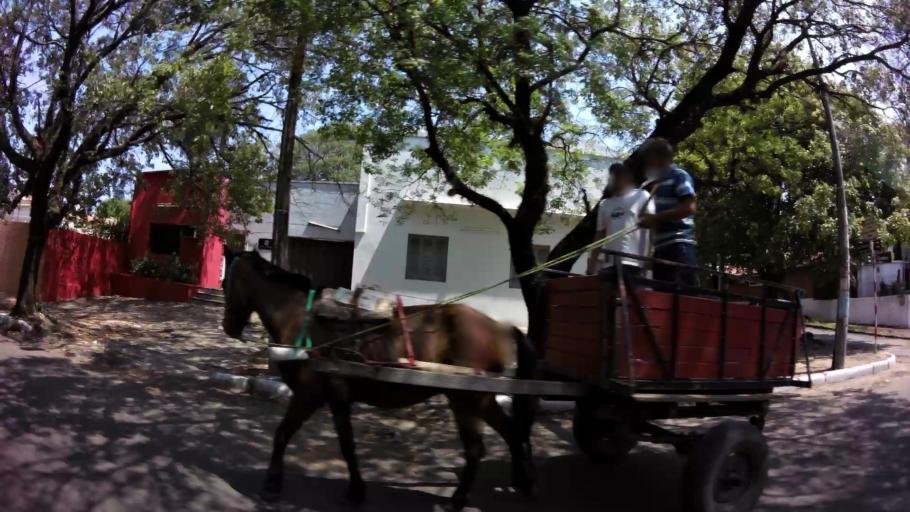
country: PY
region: Asuncion
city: Asuncion
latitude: -25.2945
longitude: -57.6528
